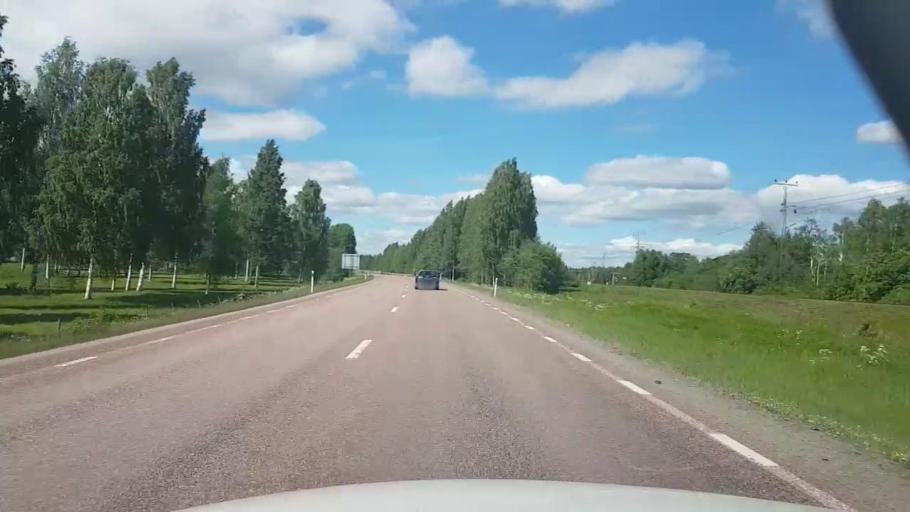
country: SE
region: Gaevleborg
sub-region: Ljusdals Kommun
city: Jaervsoe
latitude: 61.7554
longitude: 16.1611
